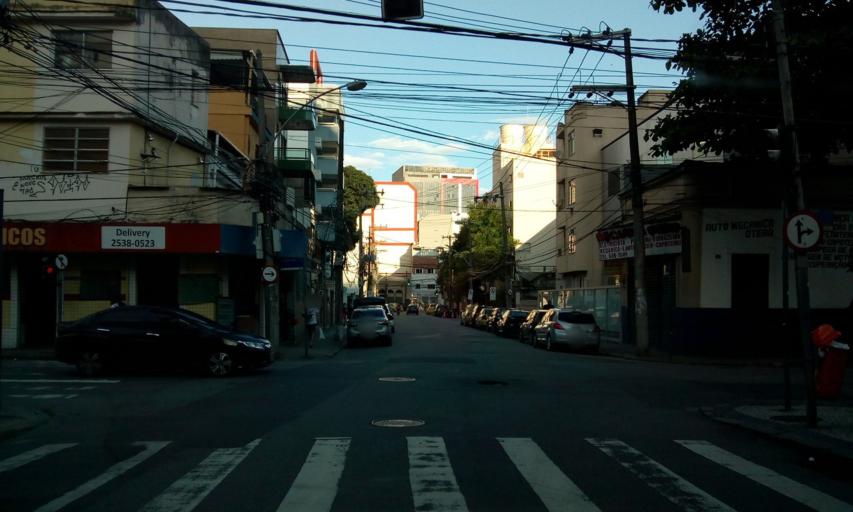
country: BR
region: Rio de Janeiro
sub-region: Rio De Janeiro
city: Rio de Janeiro
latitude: -22.9462
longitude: -43.1873
